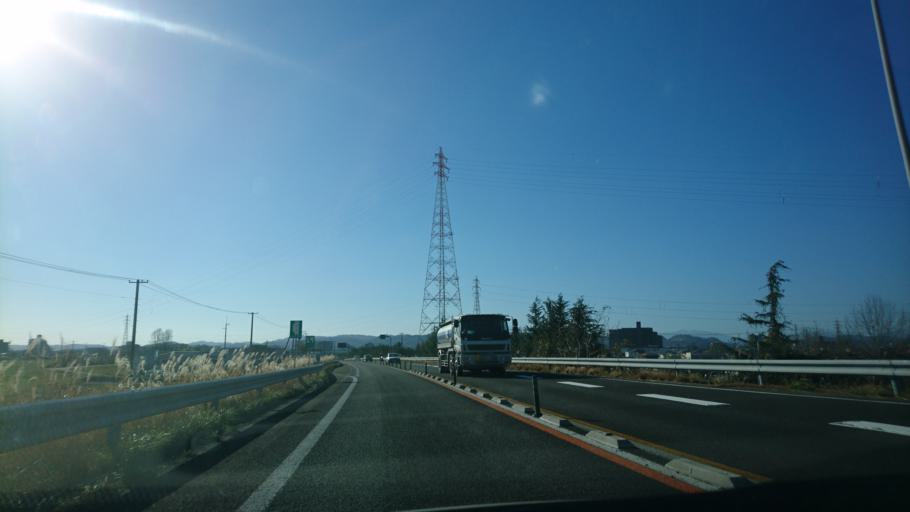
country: JP
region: Miyagi
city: Sendai
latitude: 38.2119
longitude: 140.9006
